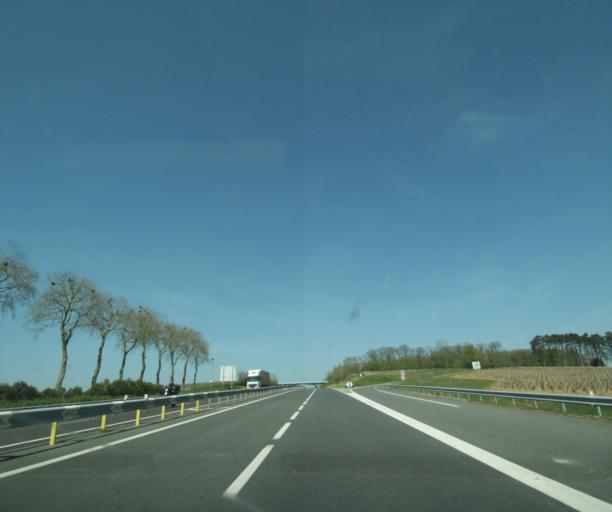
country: FR
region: Bourgogne
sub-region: Departement de la Nievre
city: Pouilly-sur-Loire
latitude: 47.2972
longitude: 2.9532
